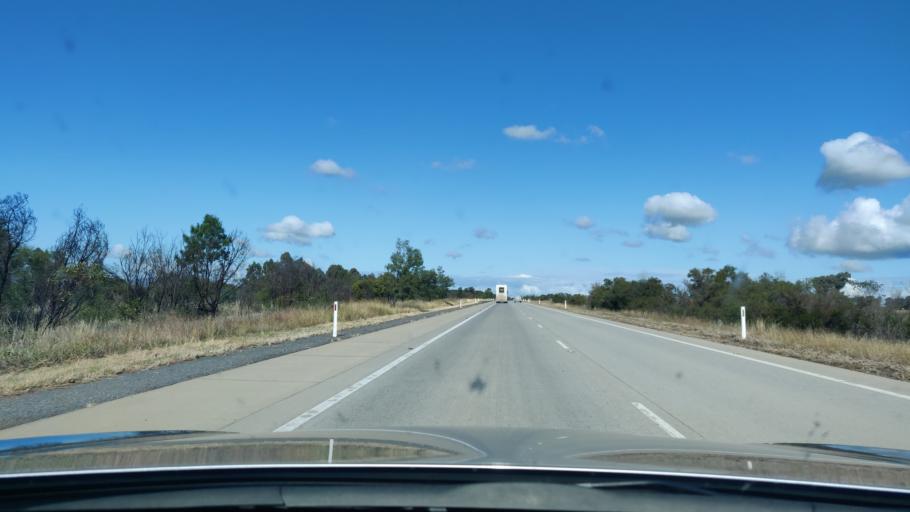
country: AU
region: New South Wales
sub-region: Greater Hume Shire
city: Jindera
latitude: -35.9526
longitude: 147.0043
